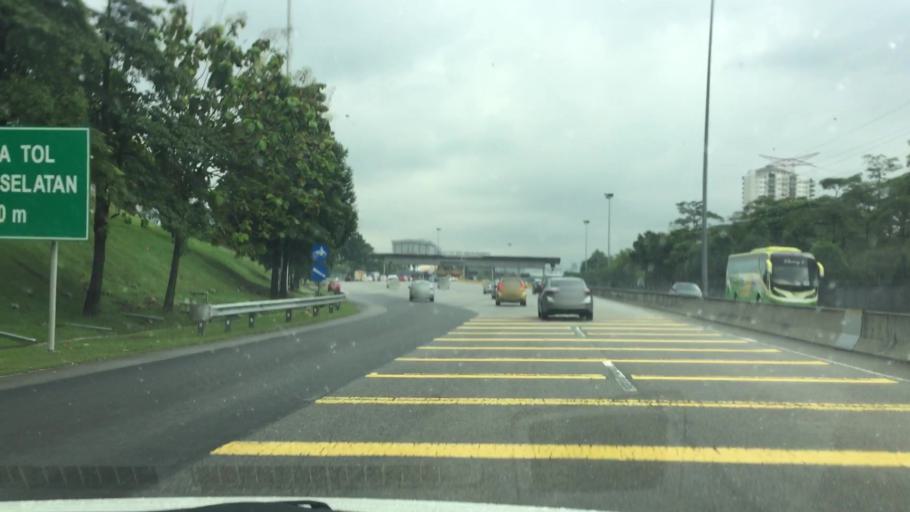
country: MY
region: Kuala Lumpur
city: Kuala Lumpur
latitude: 3.1079
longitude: 101.7101
